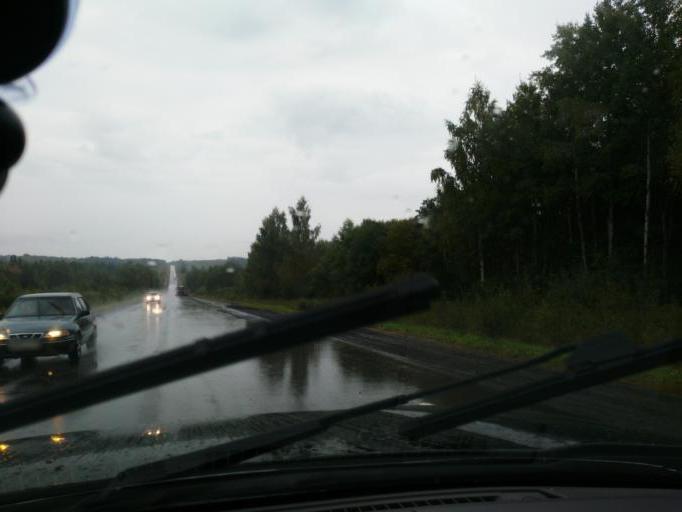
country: RU
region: Perm
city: Yugo-Kamskiy
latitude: 57.4789
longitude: 55.6797
